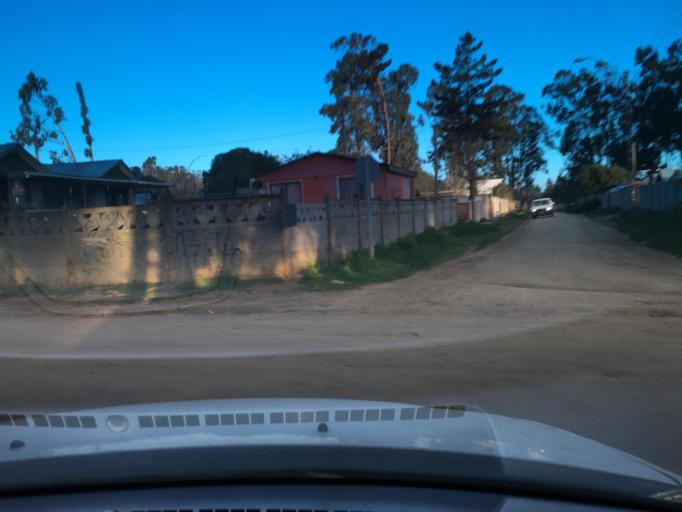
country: CL
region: Valparaiso
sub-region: San Antonio Province
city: El Tabo
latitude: -33.4539
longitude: -71.6538
